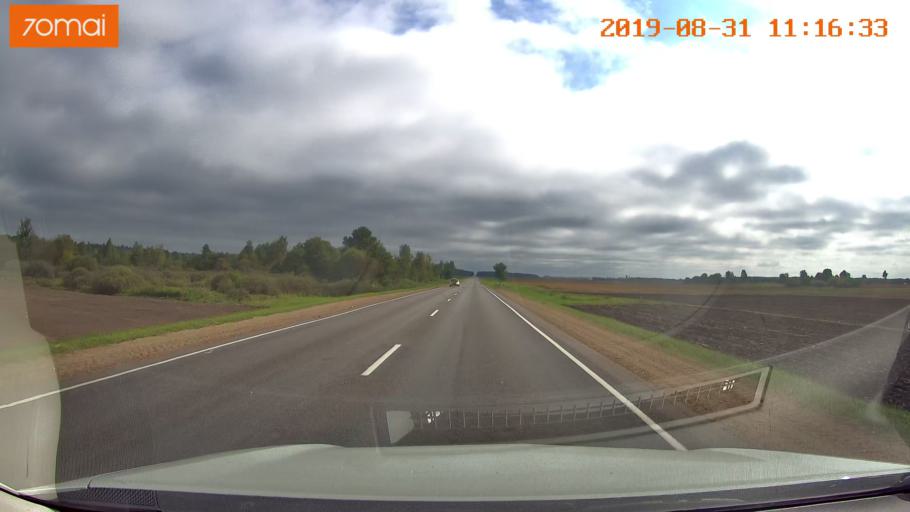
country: BY
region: Mogilev
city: Chavusy
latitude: 53.8075
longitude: 30.8824
